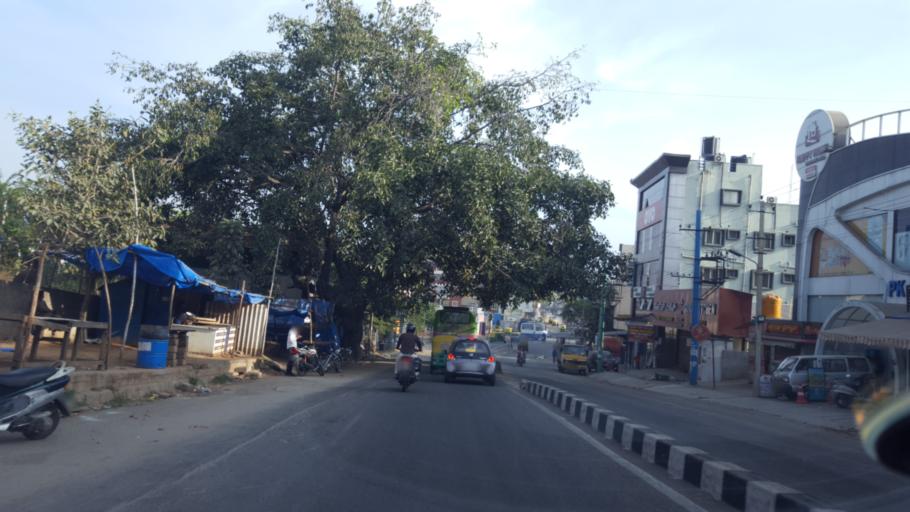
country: IN
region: Karnataka
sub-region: Bangalore Urban
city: Bangalore
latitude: 12.9189
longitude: 77.5135
